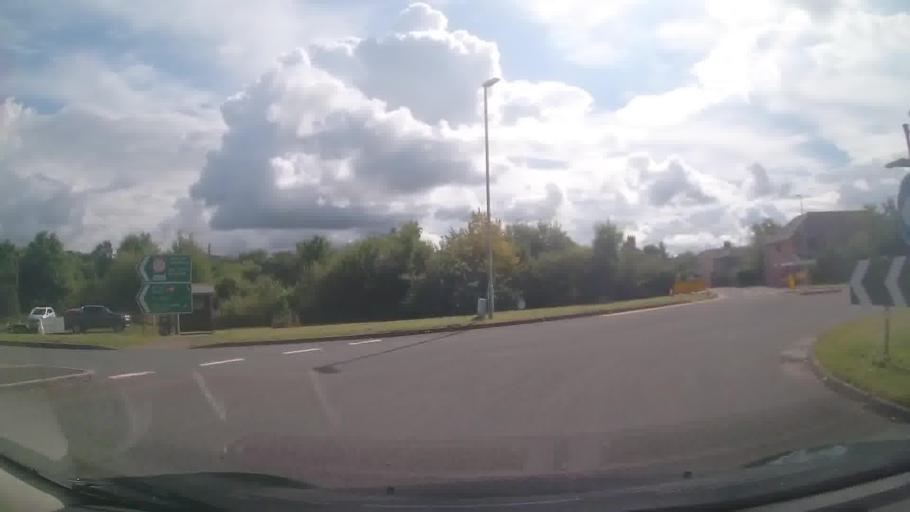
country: GB
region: Wales
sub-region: Sir Powys
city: Penybont
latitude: 52.2749
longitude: -3.3347
